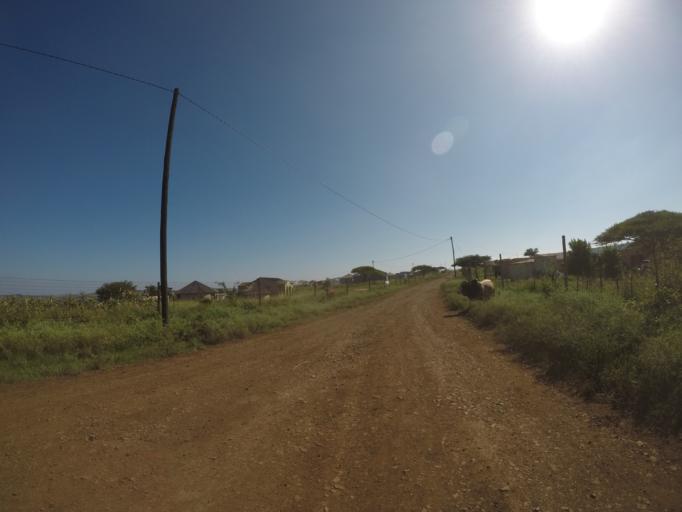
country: ZA
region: KwaZulu-Natal
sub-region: uThungulu District Municipality
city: Empangeni
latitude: -28.5705
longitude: 31.7351
